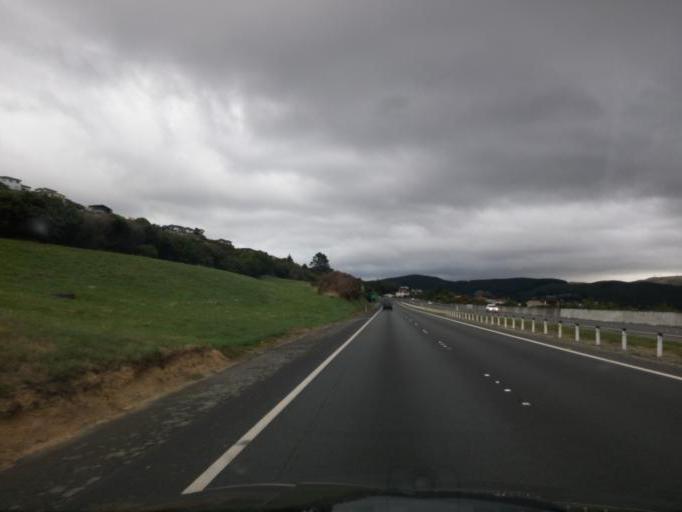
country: NZ
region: Wellington
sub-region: Porirua City
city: Porirua
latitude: -41.1650
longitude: 174.8339
